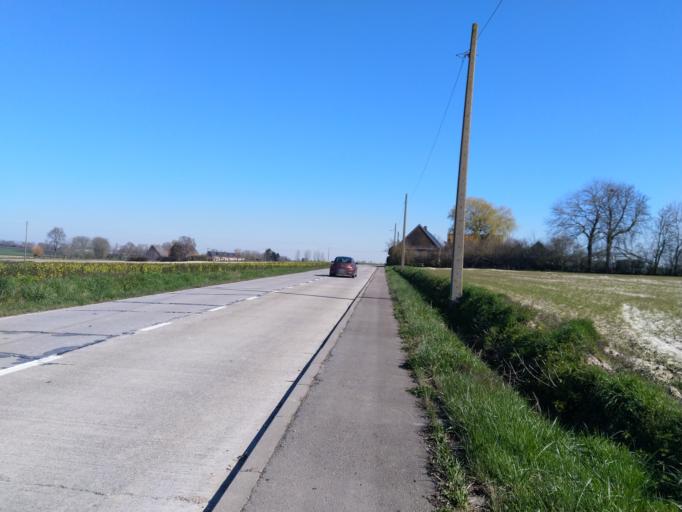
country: BE
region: Wallonia
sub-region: Province du Hainaut
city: Jurbise
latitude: 50.5629
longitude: 3.9733
